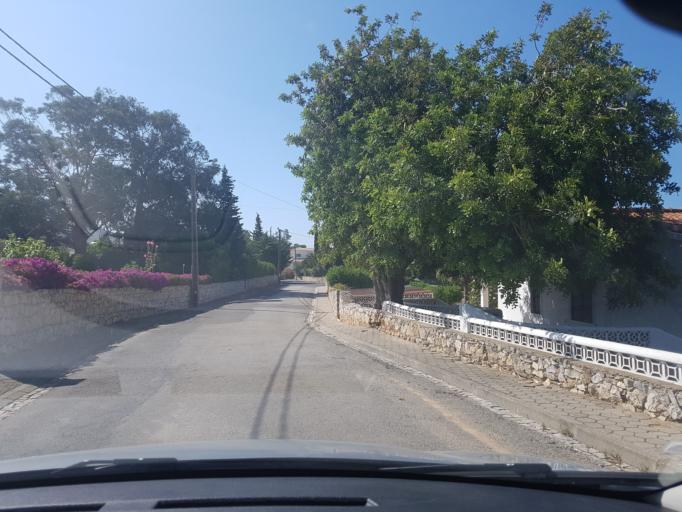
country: PT
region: Faro
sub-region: Lagoa
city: Carvoeiro
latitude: 37.0995
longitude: -8.4632
